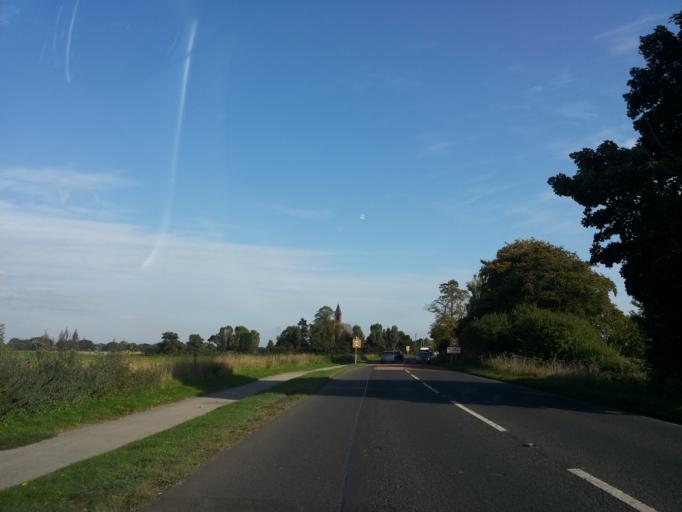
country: GB
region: England
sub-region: East Riding of Yorkshire
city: Snaith
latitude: 53.6871
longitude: -1.0043
